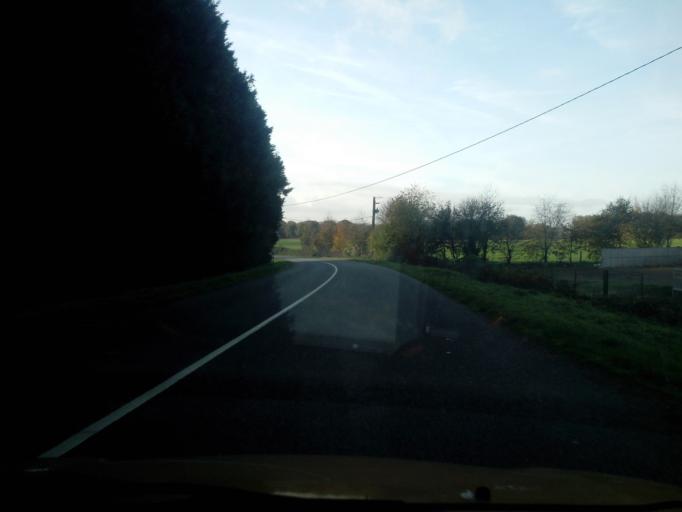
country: FR
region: Brittany
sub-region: Departement du Morbihan
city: Josselin
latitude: 47.9729
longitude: -2.5454
